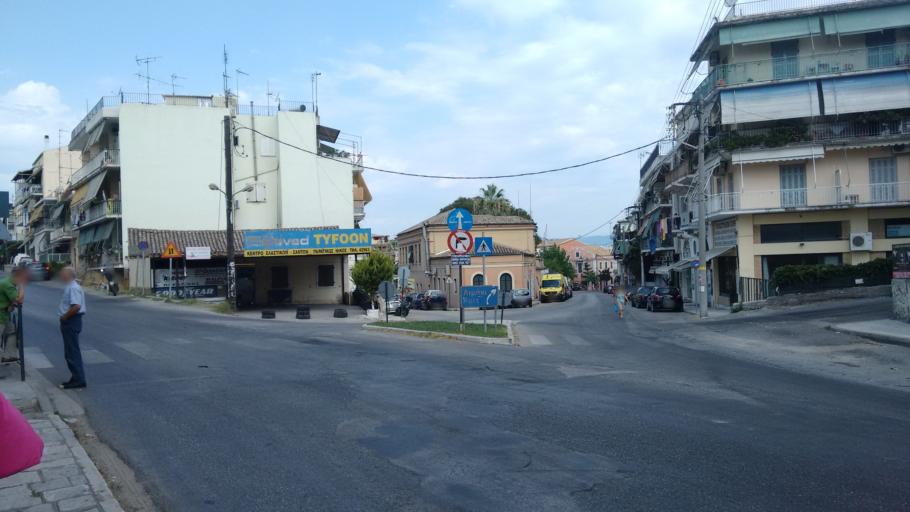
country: GR
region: Ionian Islands
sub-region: Nomos Kerkyras
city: Alepou
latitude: 39.6205
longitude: 19.9067
